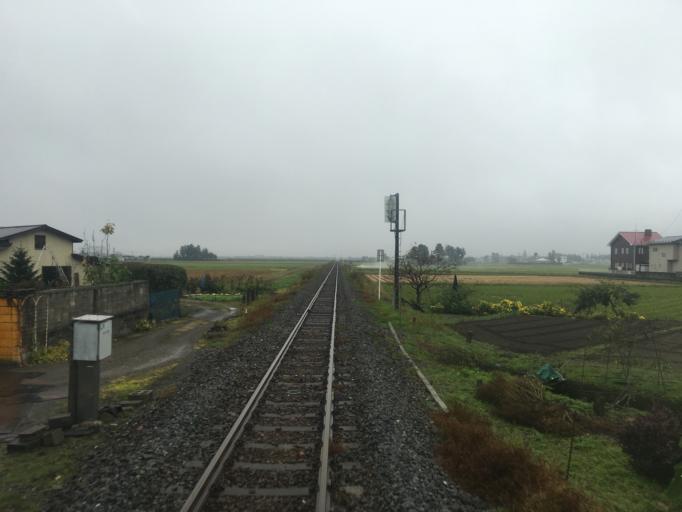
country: JP
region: Miyagi
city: Furukawa
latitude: 38.5747
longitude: 140.9014
